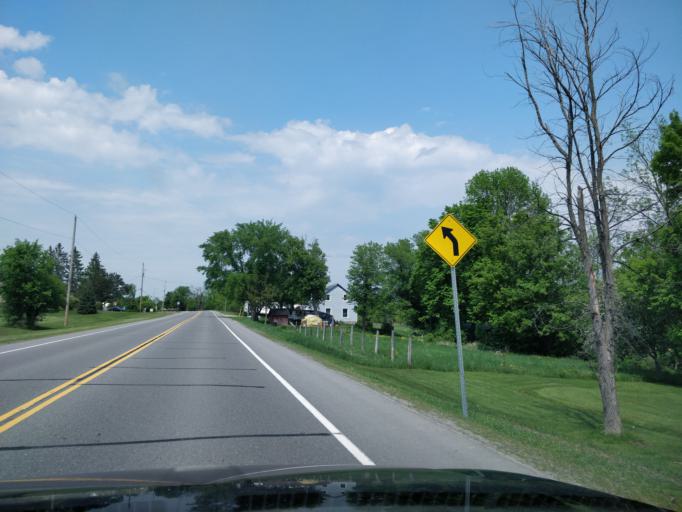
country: CA
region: Ontario
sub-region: Lanark County
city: Smiths Falls
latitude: 45.0096
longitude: -76.0809
